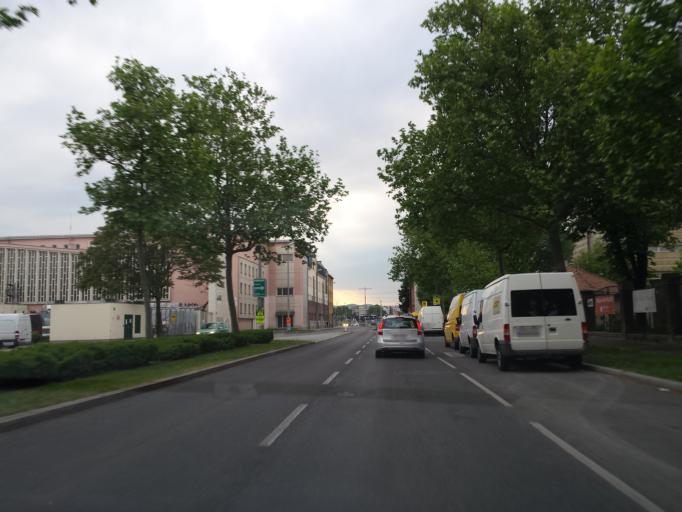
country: AT
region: Lower Austria
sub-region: Politischer Bezirk Wien-Umgebung
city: Gerasdorf bei Wien
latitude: 48.2273
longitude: 16.4603
